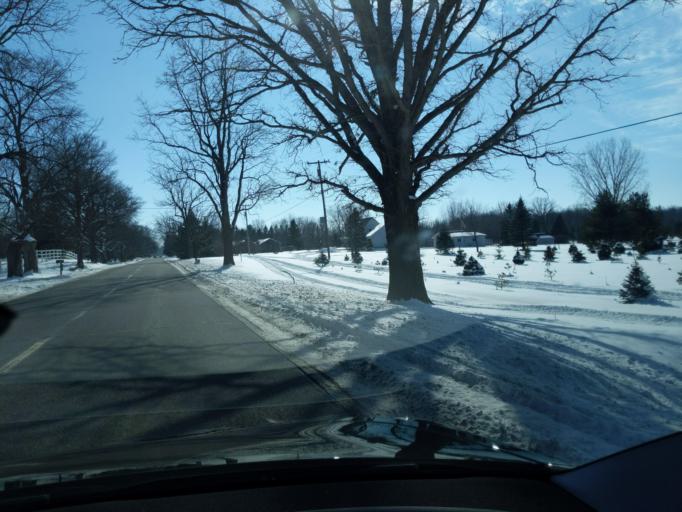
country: US
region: Michigan
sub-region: Livingston County
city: Fowlerville
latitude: 42.6089
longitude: -84.0712
